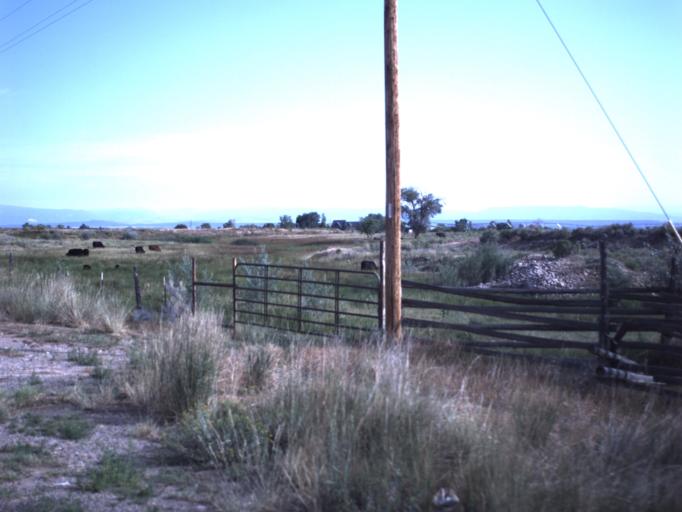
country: US
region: Utah
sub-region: Duchesne County
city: Duchesne
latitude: 40.3123
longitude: -110.2490
